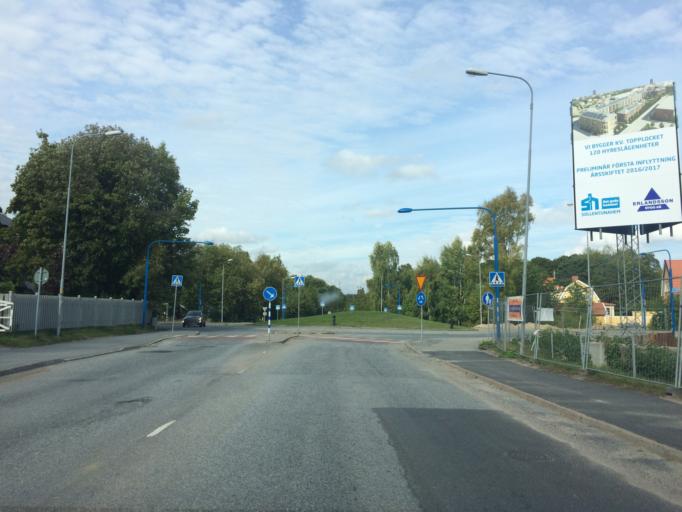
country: SE
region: Stockholm
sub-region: Sollentuna Kommun
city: Sollentuna
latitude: 59.4291
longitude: 17.9352
